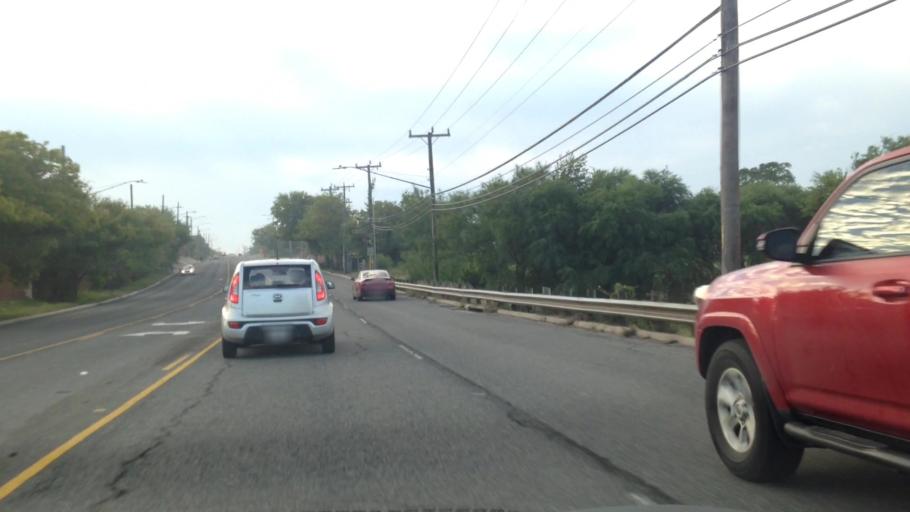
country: US
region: Texas
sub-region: Bexar County
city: Live Oak
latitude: 29.5605
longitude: -98.3608
